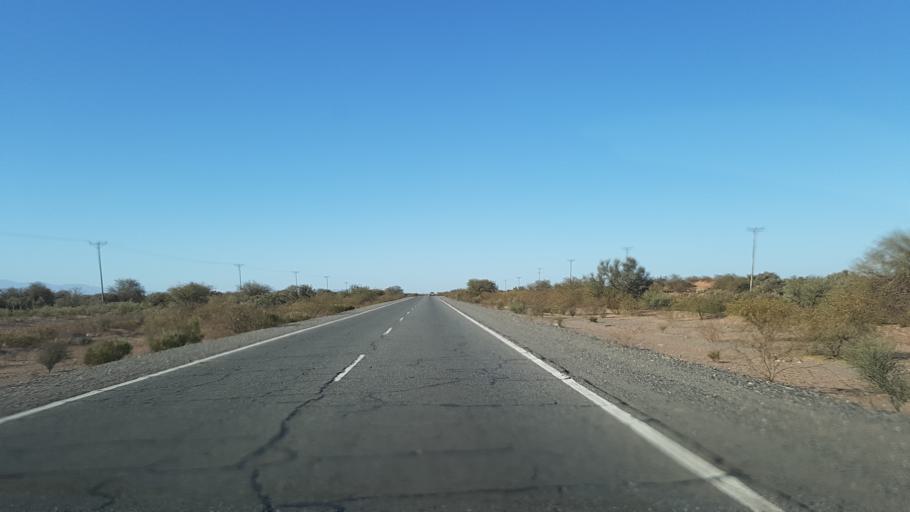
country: AR
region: San Juan
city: Caucete
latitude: -31.6050
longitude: -67.7103
